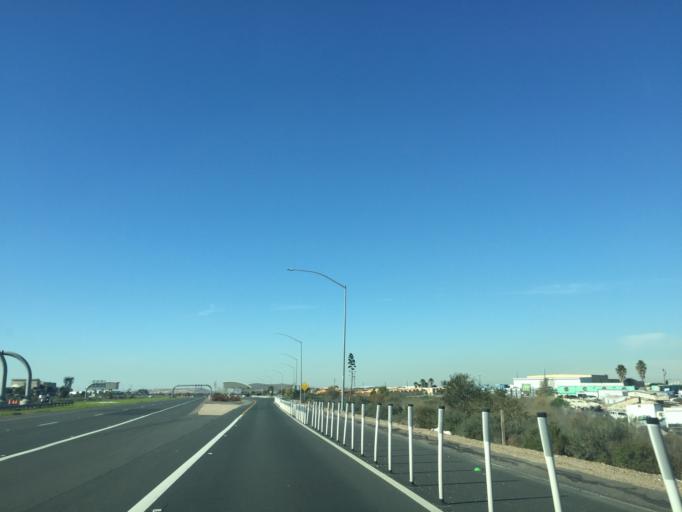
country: MX
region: Baja California
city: Tijuana
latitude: 32.5756
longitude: -116.9550
